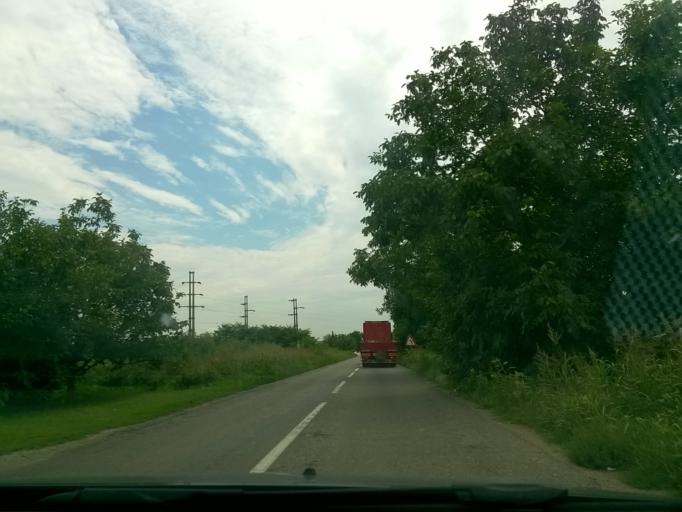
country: RS
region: Autonomna Pokrajina Vojvodina
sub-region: Srednjebanatski Okrug
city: Zrenjanin
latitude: 45.3841
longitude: 20.4286
